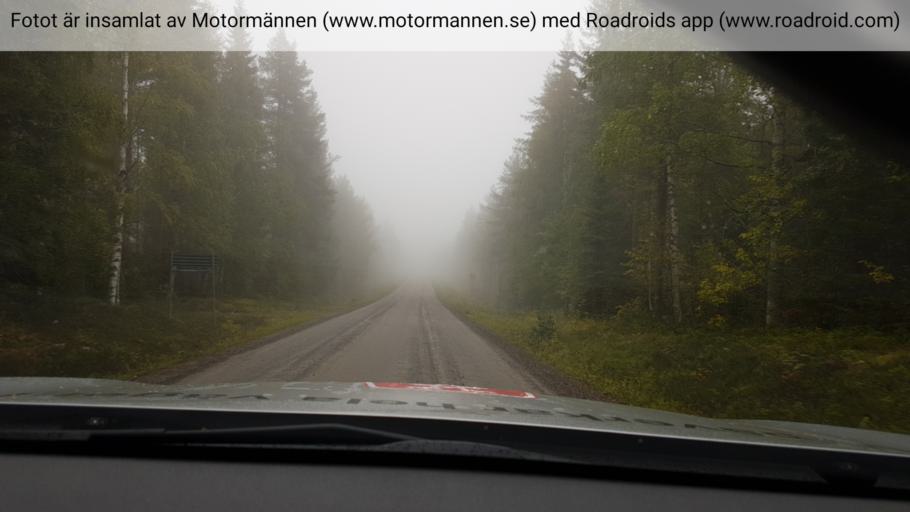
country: SE
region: Vaesterbotten
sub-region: Umea Kommun
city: Ersmark
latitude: 64.0885
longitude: 20.2233
